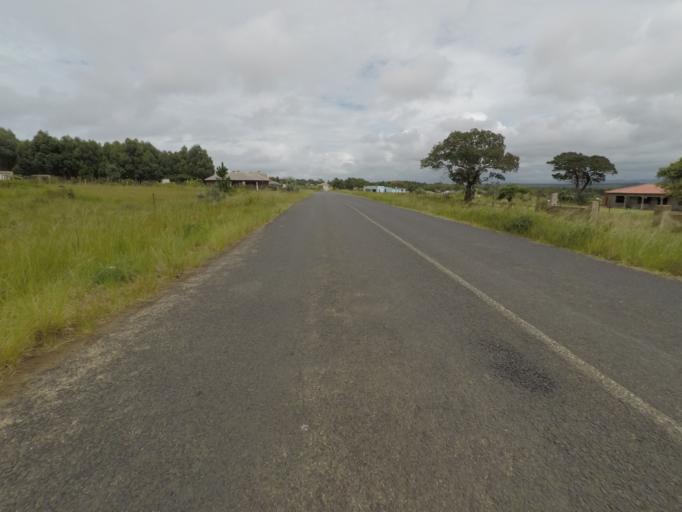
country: ZA
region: KwaZulu-Natal
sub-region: uThungulu District Municipality
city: eSikhawini
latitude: -28.9134
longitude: 31.8526
